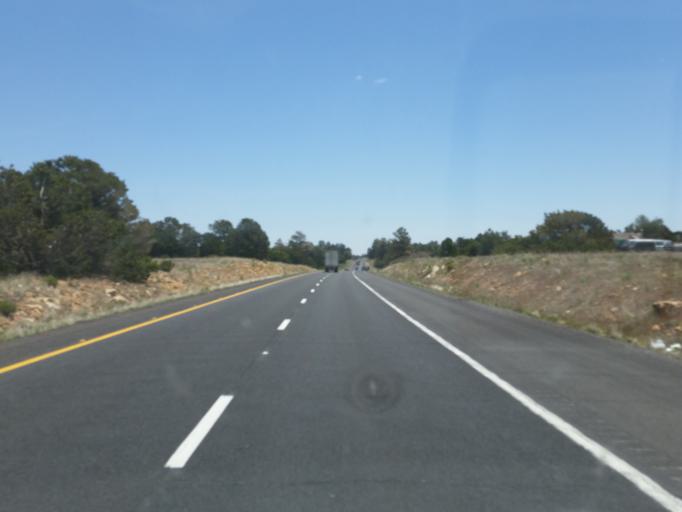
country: US
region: Arizona
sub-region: Coconino County
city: Flagstaff
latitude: 35.2174
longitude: -111.5578
